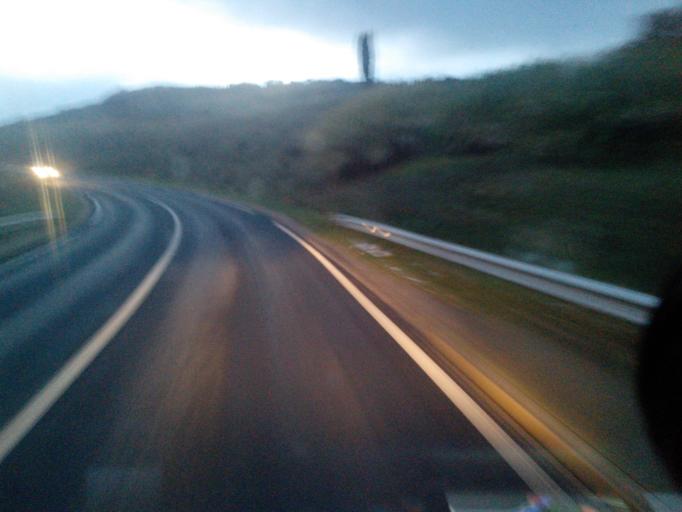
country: FR
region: Languedoc-Roussillon
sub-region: Departement de l'Herault
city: Nebian
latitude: 43.6437
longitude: 3.4473
